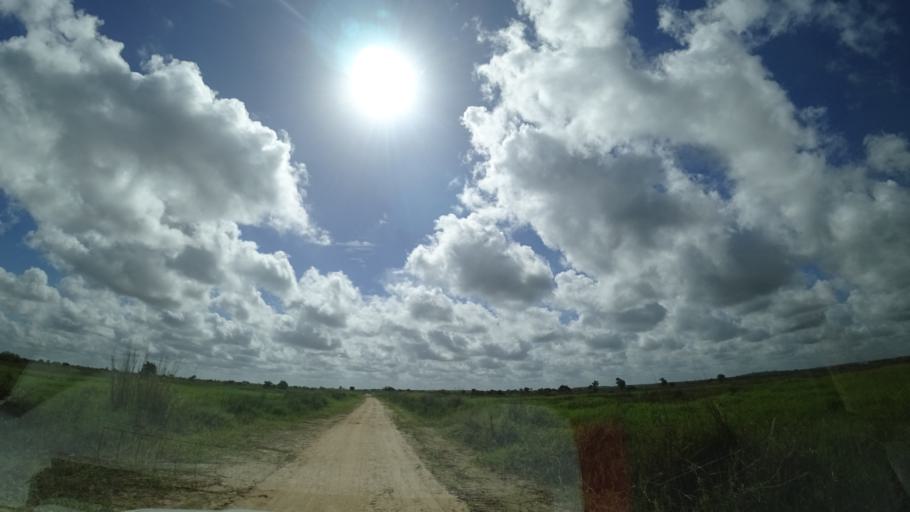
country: MZ
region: Sofala
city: Dondo
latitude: -19.3933
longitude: 34.5747
